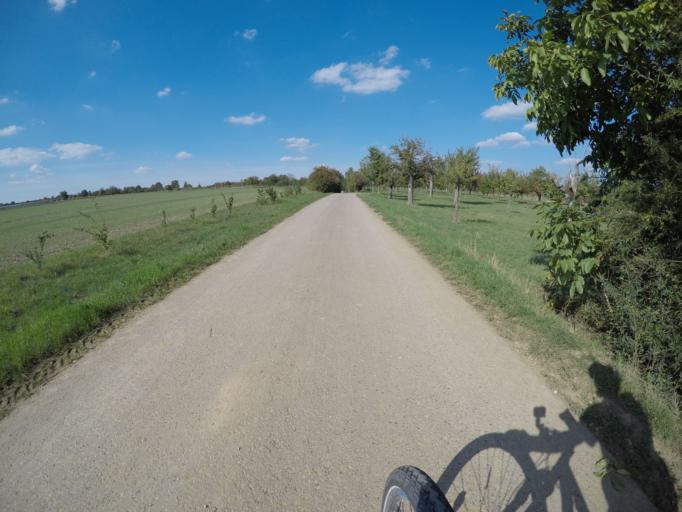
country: DE
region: Baden-Wuerttemberg
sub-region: Regierungsbezirk Stuttgart
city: Neuhausen auf den Fildern
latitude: 48.6922
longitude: 9.2800
